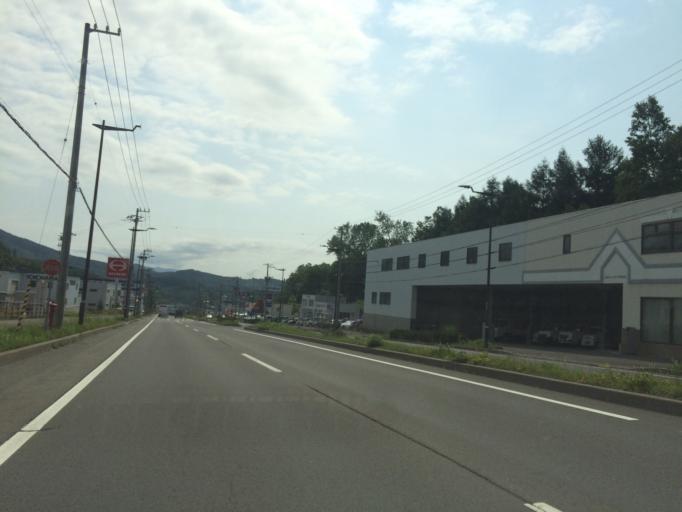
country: JP
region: Hokkaido
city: Otaru
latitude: 43.2166
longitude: 140.9433
